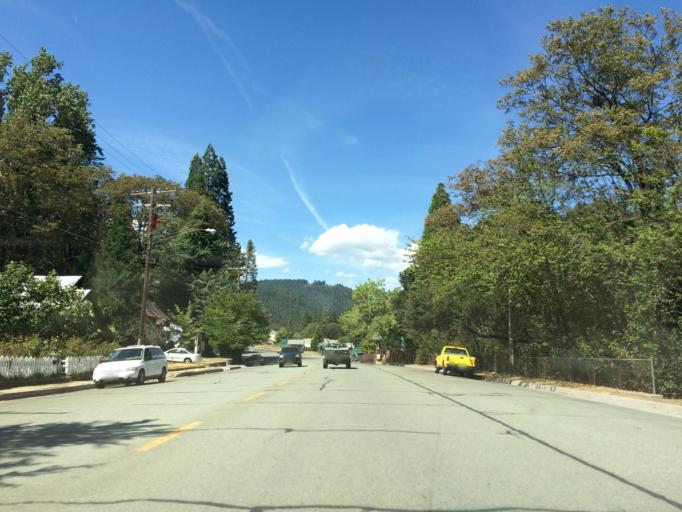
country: US
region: California
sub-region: Siskiyou County
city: Dunsmuir
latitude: 41.2162
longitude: -122.2728
